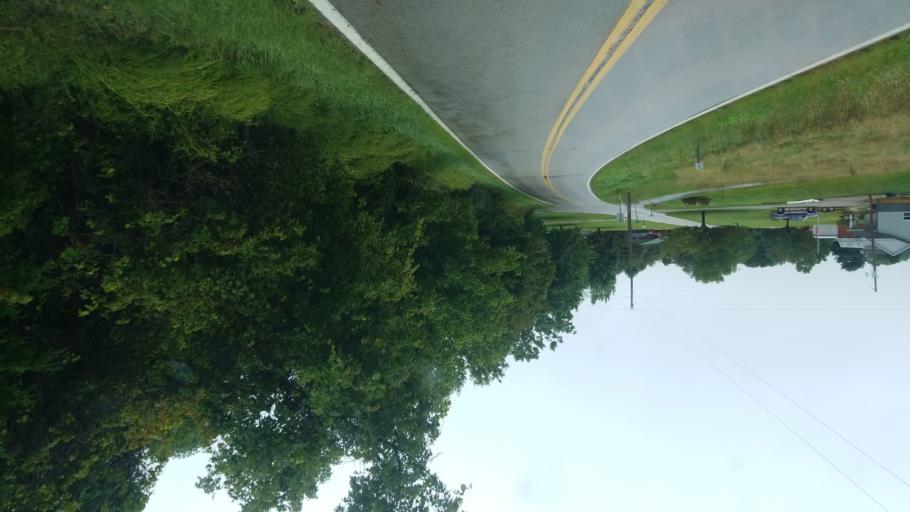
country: US
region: Ohio
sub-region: Adams County
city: West Union
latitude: 38.7287
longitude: -83.5178
